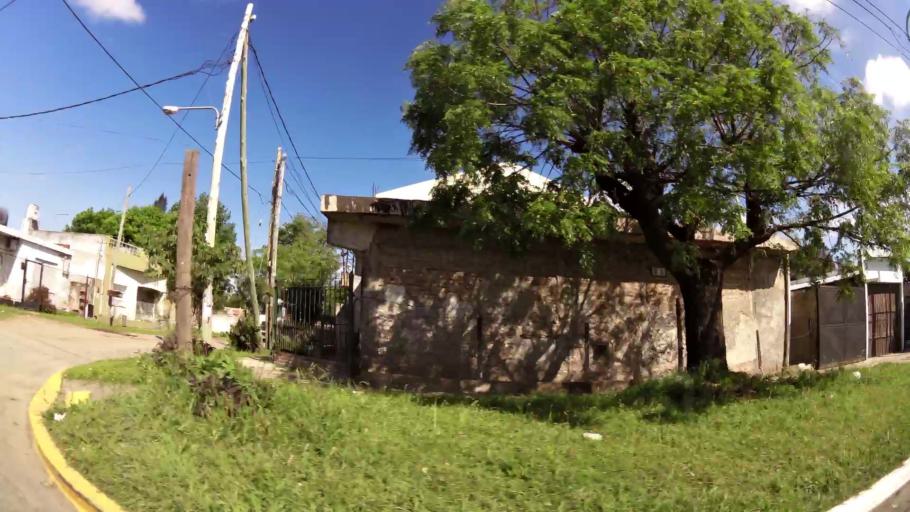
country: AR
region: Buenos Aires
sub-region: Partido de Quilmes
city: Quilmes
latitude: -34.7953
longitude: -58.2547
